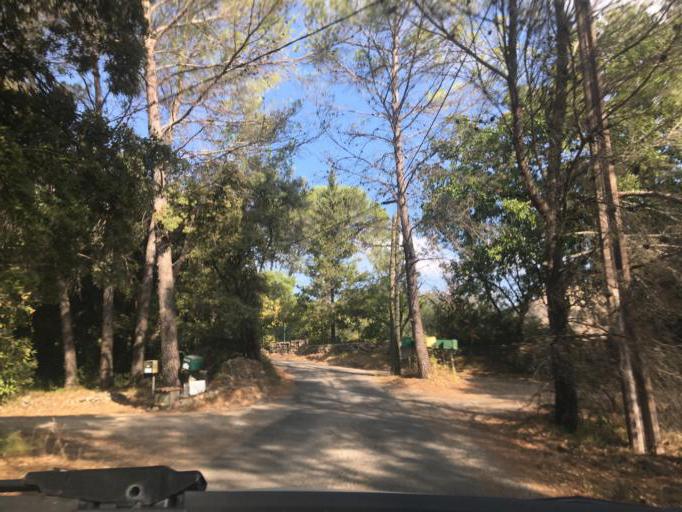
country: FR
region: Provence-Alpes-Cote d'Azur
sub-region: Departement du Var
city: Lorgues
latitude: 43.4917
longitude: 6.3958
